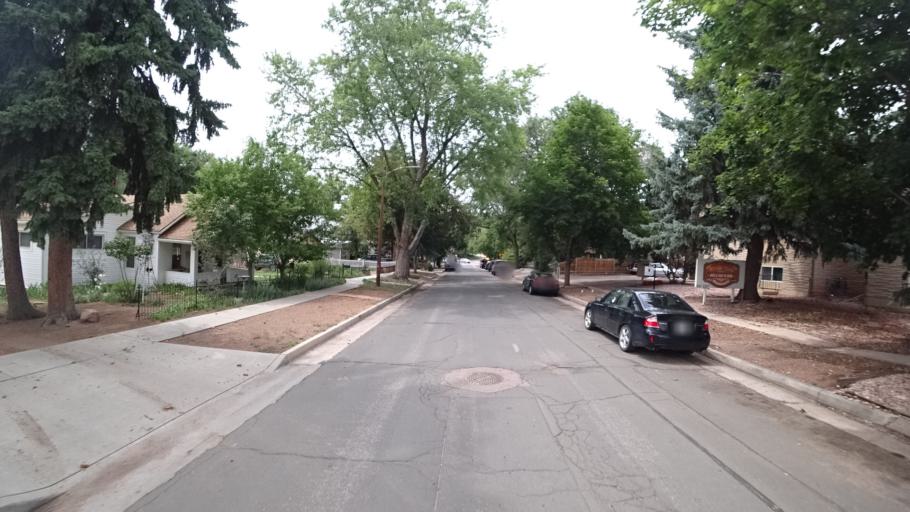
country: US
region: Colorado
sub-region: El Paso County
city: Manitou Springs
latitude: 38.8543
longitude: -104.8691
